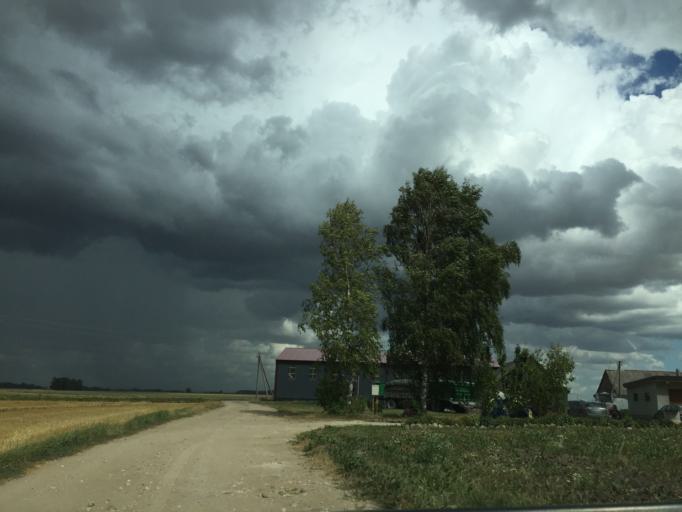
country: LT
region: Siauliu apskritis
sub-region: Joniskis
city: Joniskis
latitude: 56.2851
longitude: 23.7241
